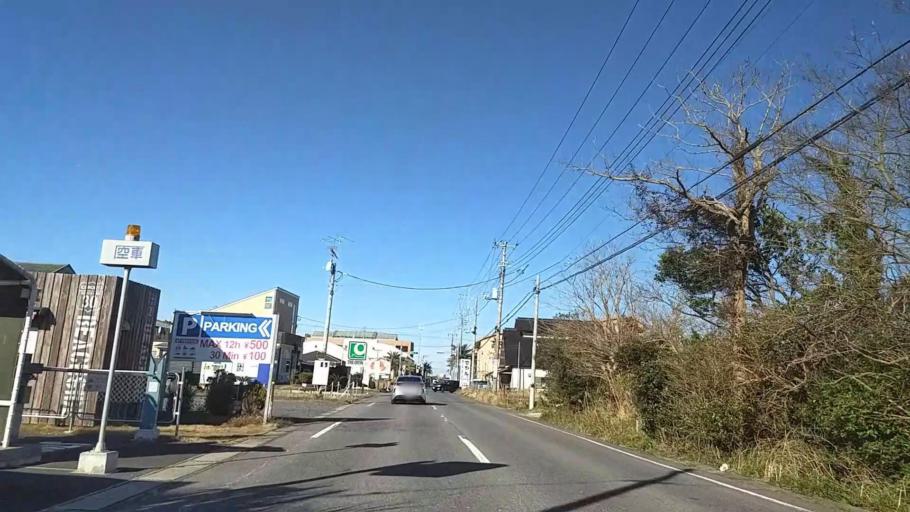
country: JP
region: Chiba
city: Mobara
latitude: 35.3602
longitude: 140.3882
